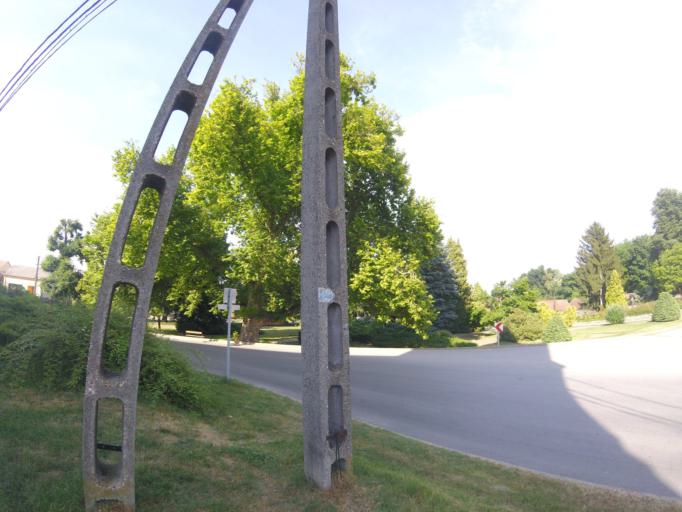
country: HU
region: Baranya
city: Sellye
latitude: 45.8714
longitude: 17.8459
